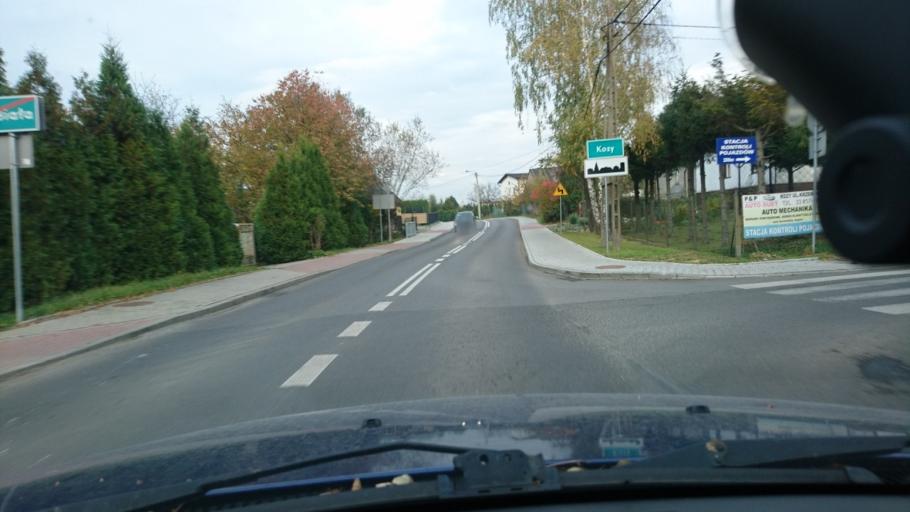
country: PL
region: Silesian Voivodeship
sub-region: Powiat bielski
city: Kozy
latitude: 49.8420
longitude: 19.1155
